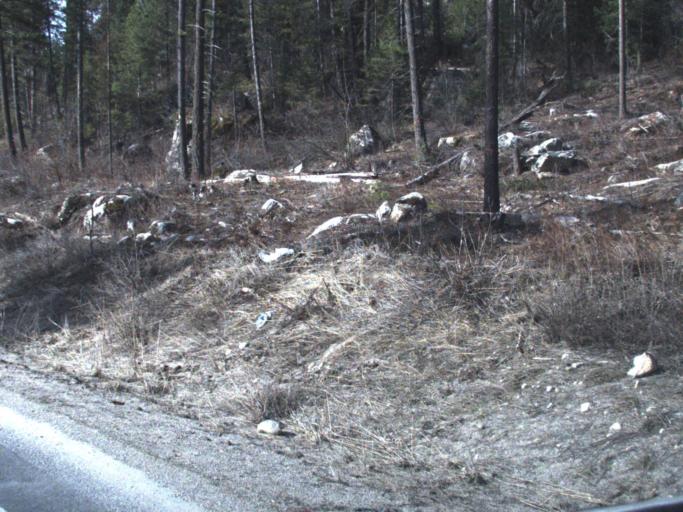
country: US
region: Washington
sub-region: Stevens County
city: Chewelah
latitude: 48.5083
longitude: -117.6639
